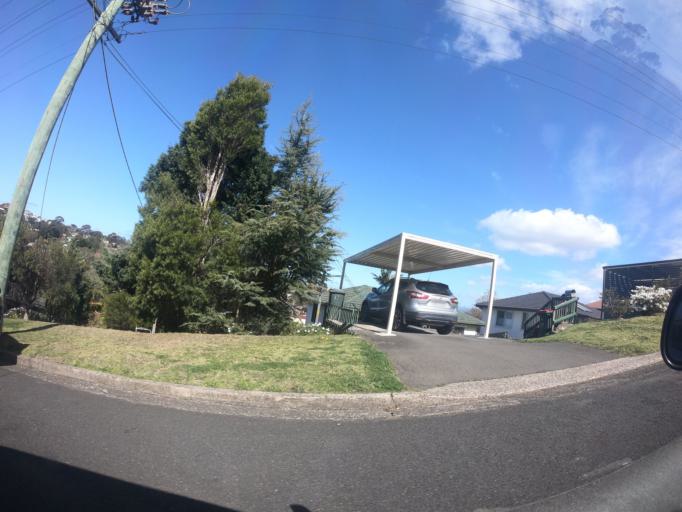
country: AU
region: New South Wales
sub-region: Wollongong
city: Berkeley
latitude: -34.4727
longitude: 150.8410
